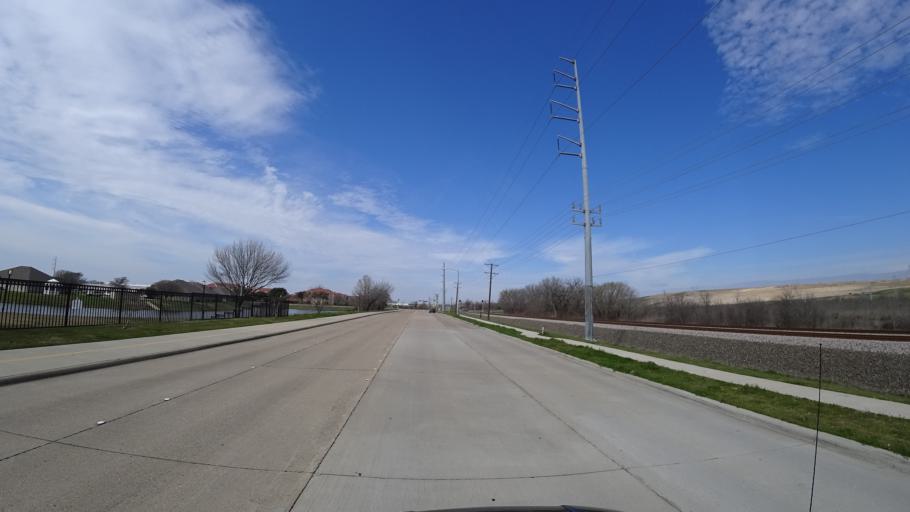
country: US
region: Texas
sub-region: Denton County
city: Lewisville
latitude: 33.0118
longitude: -96.9601
